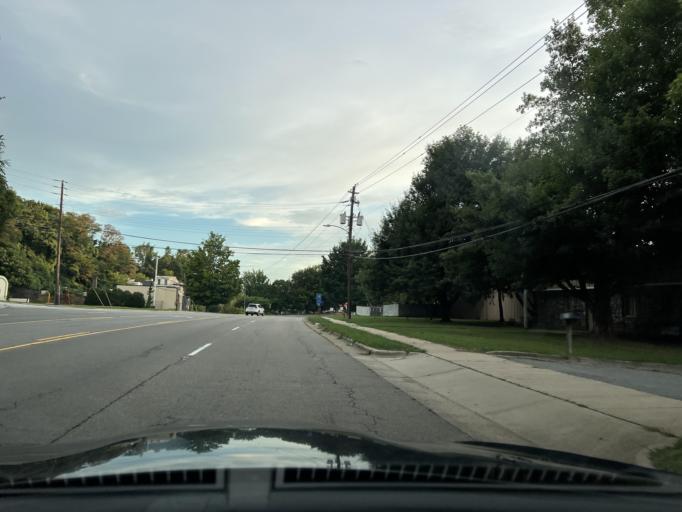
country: US
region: North Carolina
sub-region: Buncombe County
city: Asheville
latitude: 35.5901
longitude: -82.5499
